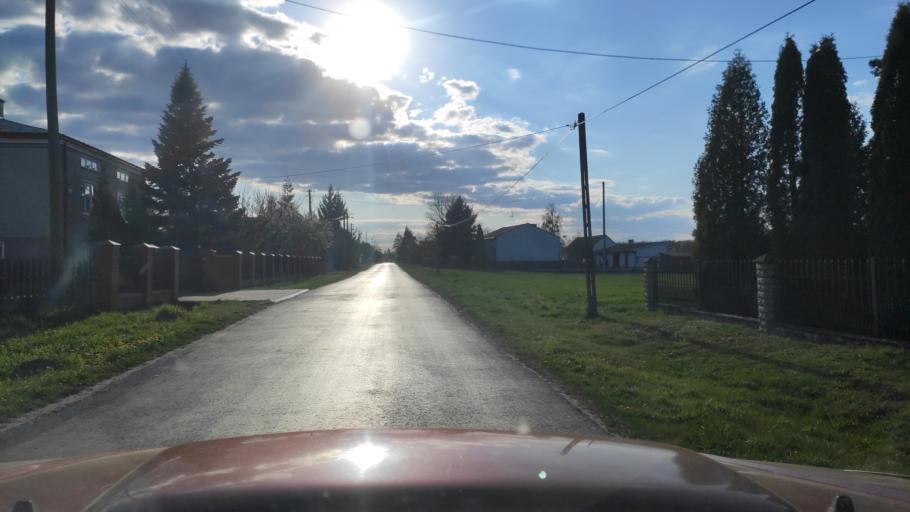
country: PL
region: Masovian Voivodeship
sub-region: Powiat zwolenski
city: Zwolen
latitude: 51.3843
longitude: 21.5703
